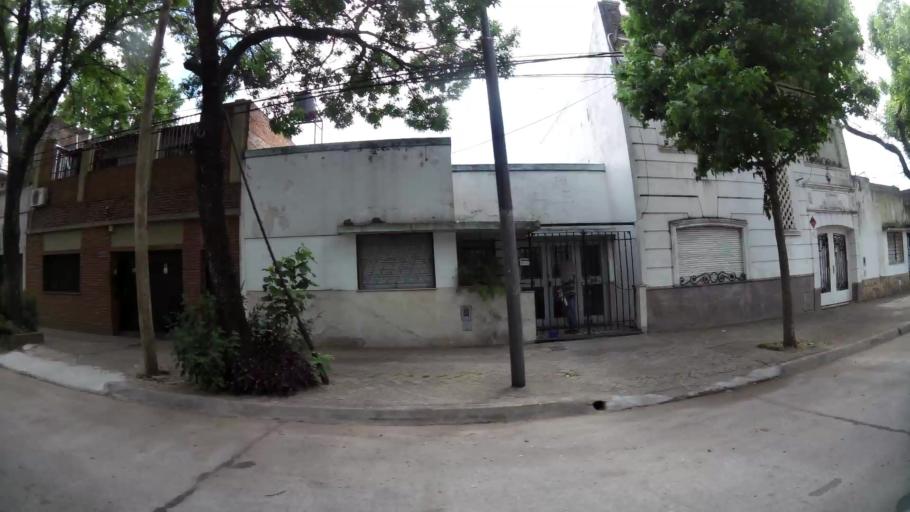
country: AR
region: Santa Fe
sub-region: Departamento de Rosario
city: Rosario
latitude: -32.9802
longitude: -60.6398
